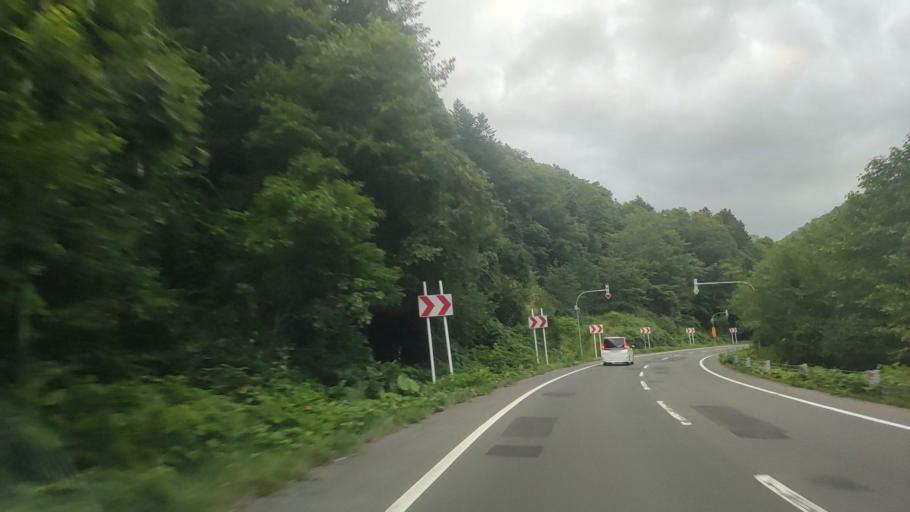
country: JP
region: Hokkaido
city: Shimo-furano
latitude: 43.3455
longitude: 142.2847
